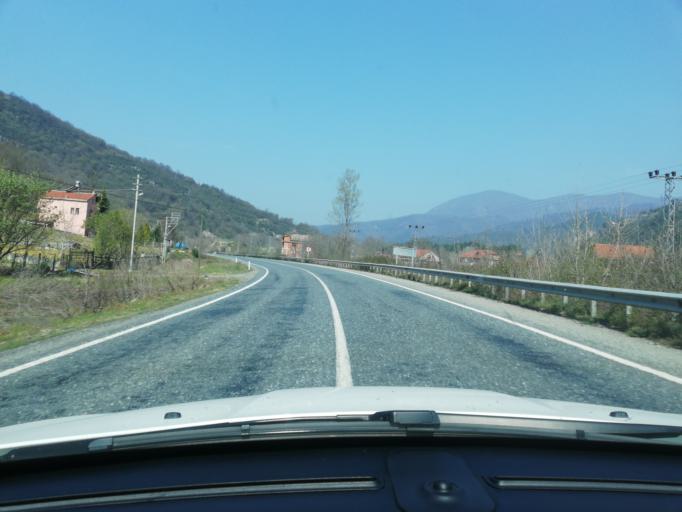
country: TR
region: Zonguldak
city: Gokcebey
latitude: 41.2230
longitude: 32.2190
